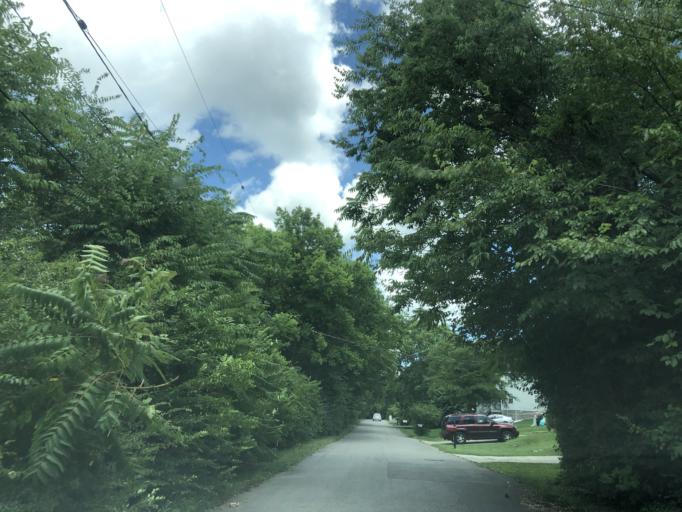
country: US
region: Tennessee
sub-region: Davidson County
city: Oak Hill
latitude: 36.0739
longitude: -86.7226
